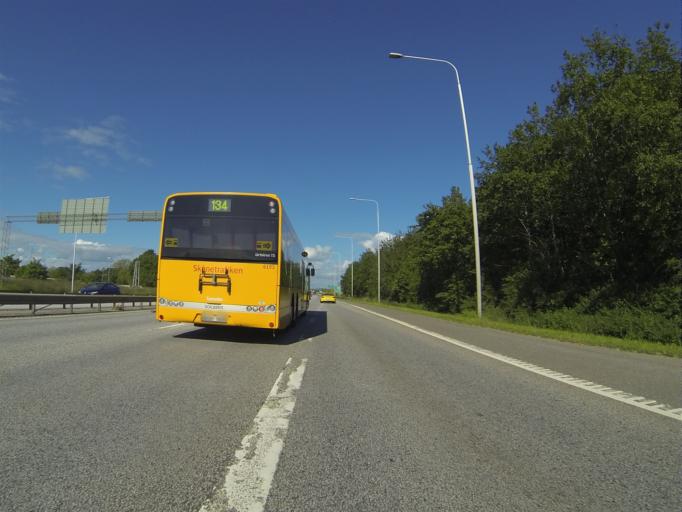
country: SE
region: Skane
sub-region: Burlovs Kommun
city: Arloev
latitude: 55.6228
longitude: 13.0647
